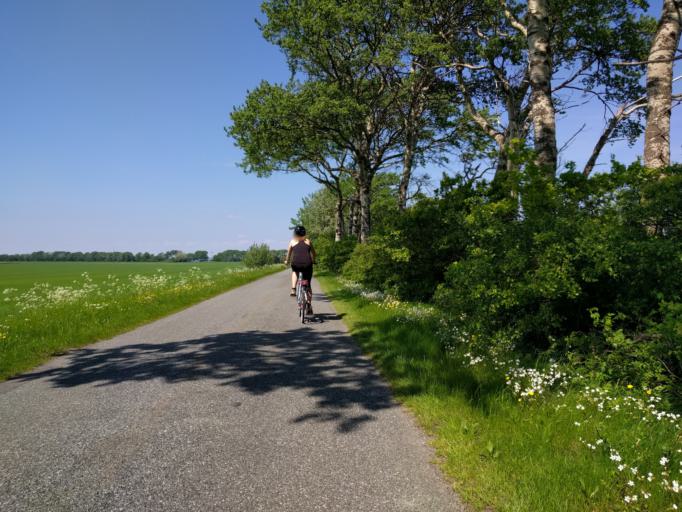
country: DK
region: Zealand
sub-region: Guldborgsund Kommune
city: Stubbekobing
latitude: 54.8789
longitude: 12.1208
